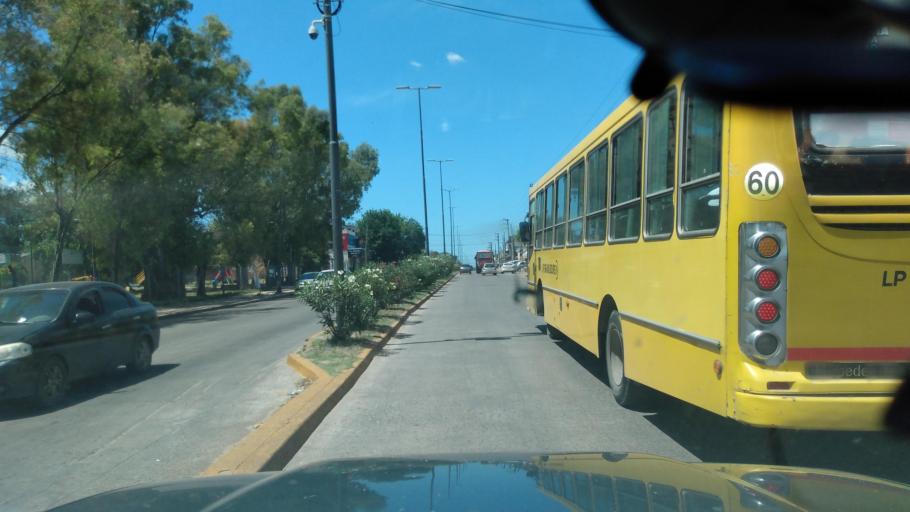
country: AR
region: Buenos Aires
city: Hurlingham
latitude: -34.5644
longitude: -58.7375
